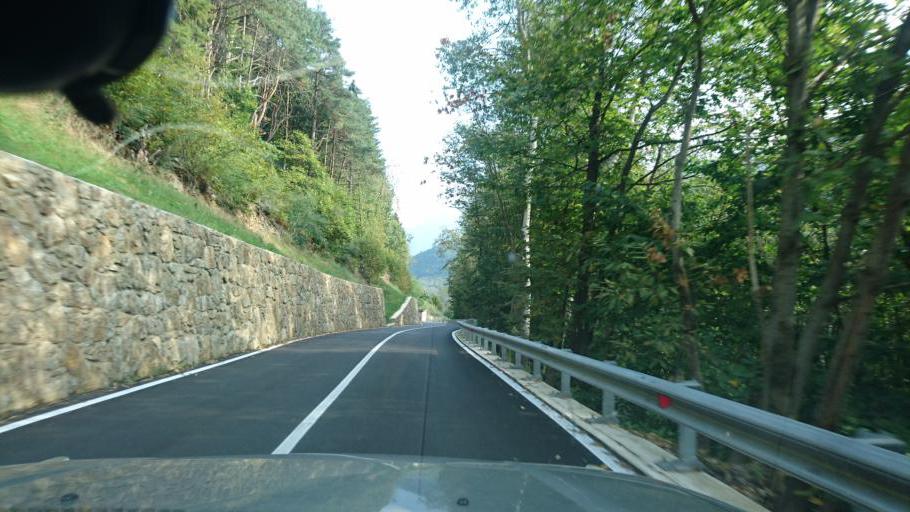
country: IT
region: Lombardy
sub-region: Provincia di Brescia
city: Paisco Loveno
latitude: 46.0929
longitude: 10.3083
